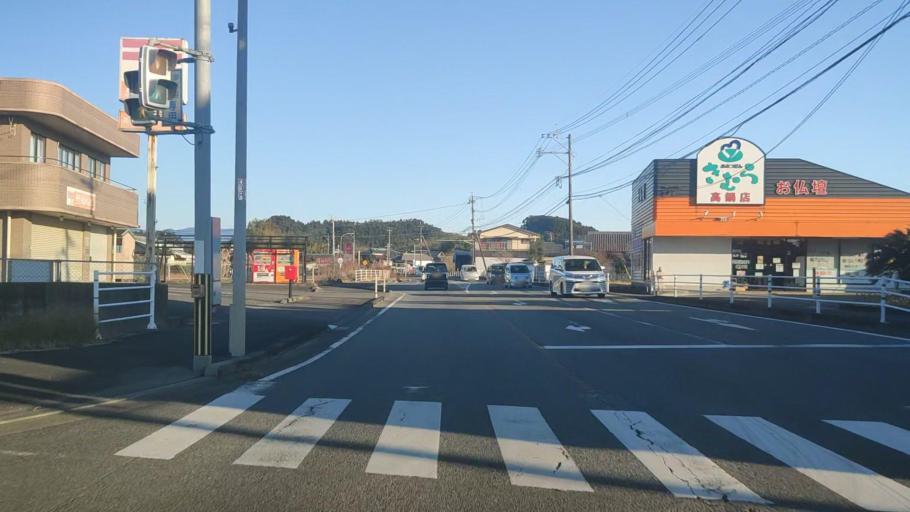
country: JP
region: Miyazaki
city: Takanabe
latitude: 32.1383
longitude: 131.5276
